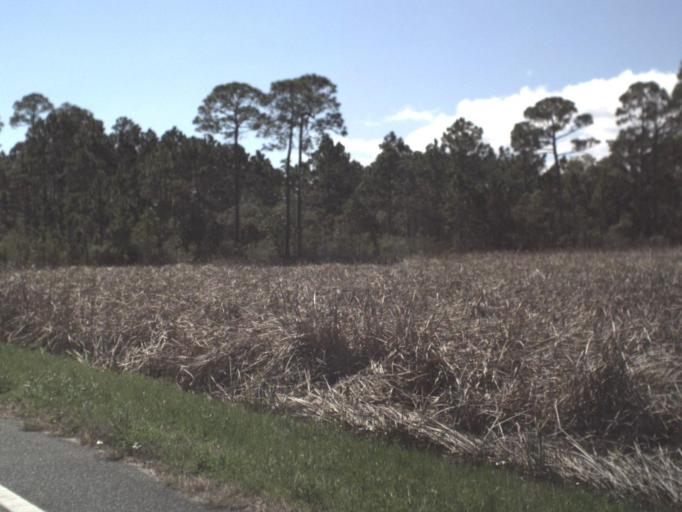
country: US
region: Florida
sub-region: Wakulla County
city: Crawfordville
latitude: 30.0130
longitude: -84.3938
